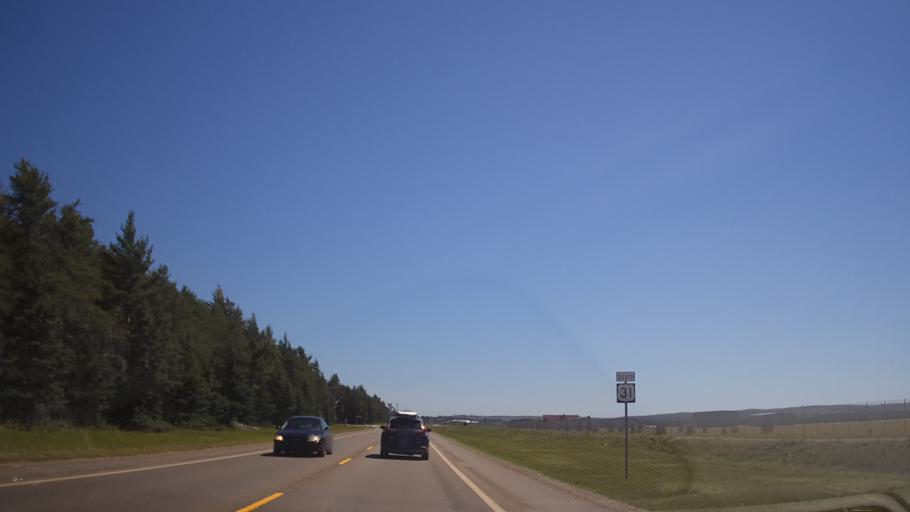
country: US
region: Michigan
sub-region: Cheboygan County
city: Indian River
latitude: 45.5797
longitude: -84.7834
